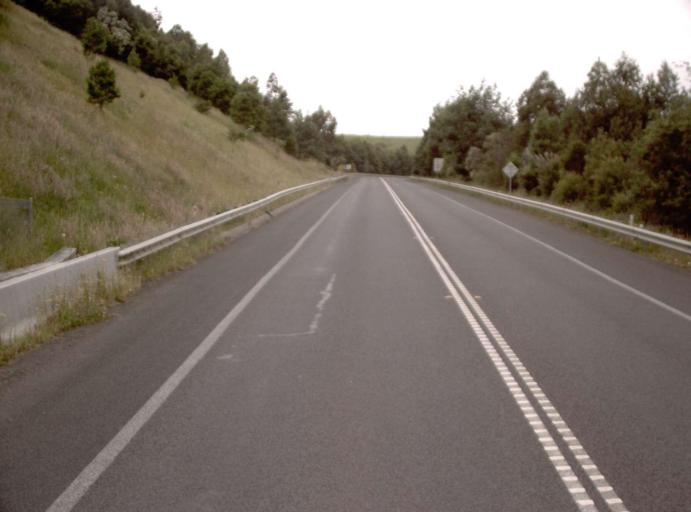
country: AU
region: Victoria
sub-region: Bass Coast
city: North Wonthaggi
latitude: -38.3773
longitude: 145.7273
